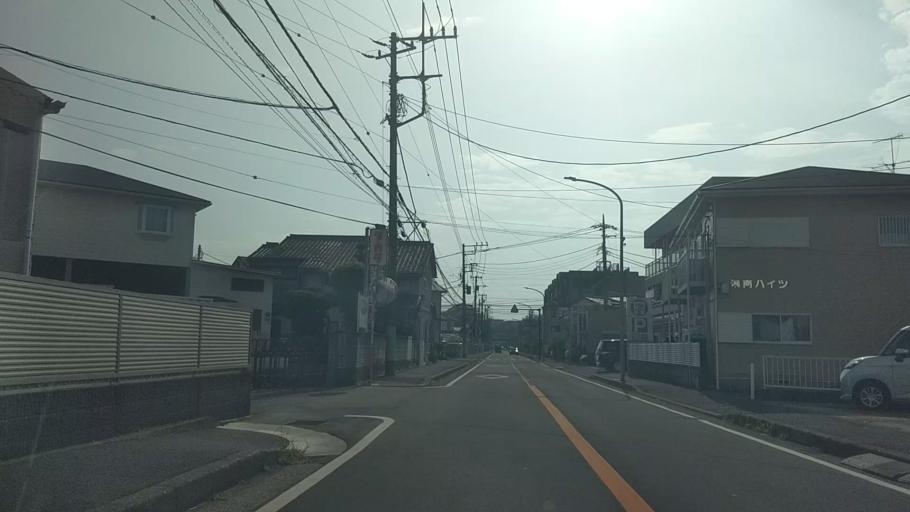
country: JP
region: Kanagawa
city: Kamakura
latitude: 35.3629
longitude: 139.5452
